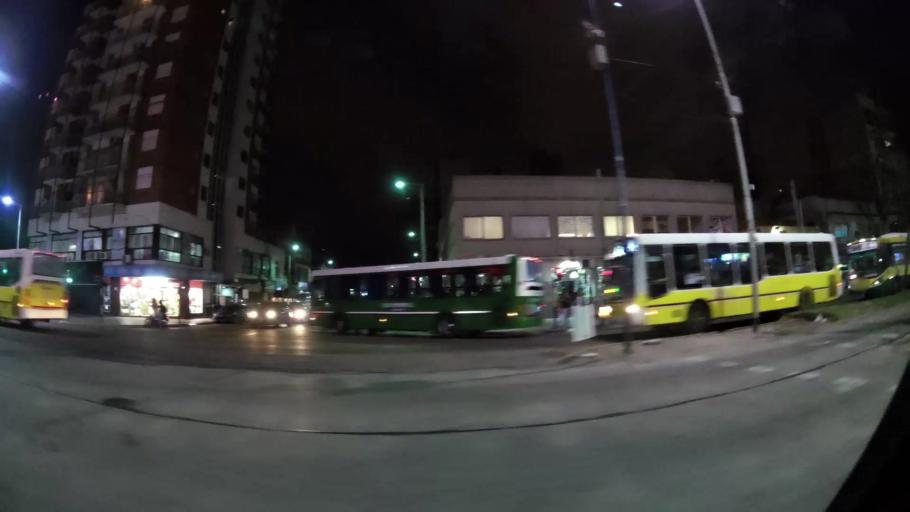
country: AR
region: Buenos Aires
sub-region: Partido de Avellaneda
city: Avellaneda
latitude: -34.7040
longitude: -58.3176
